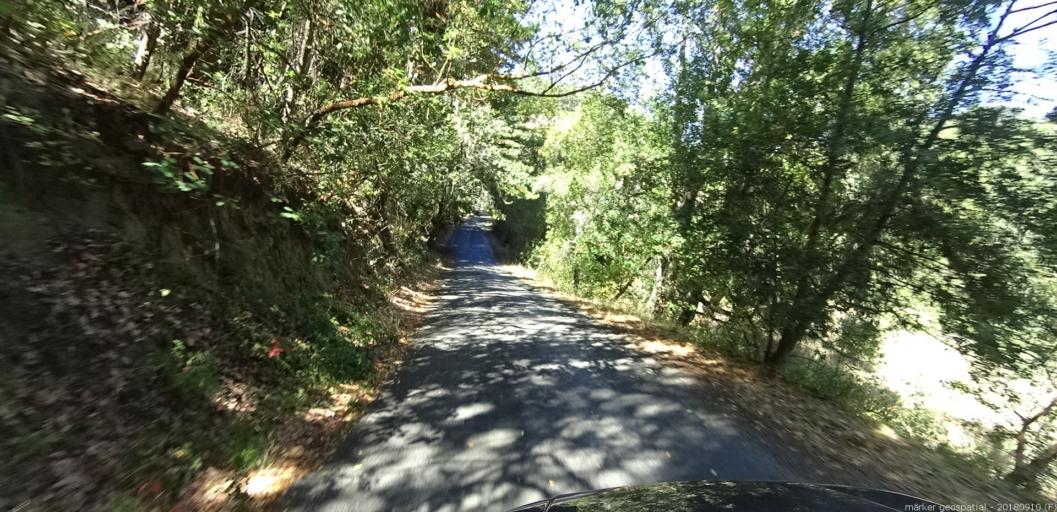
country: US
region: California
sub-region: Monterey County
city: Carmel Valley Village
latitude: 36.4278
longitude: -121.7878
